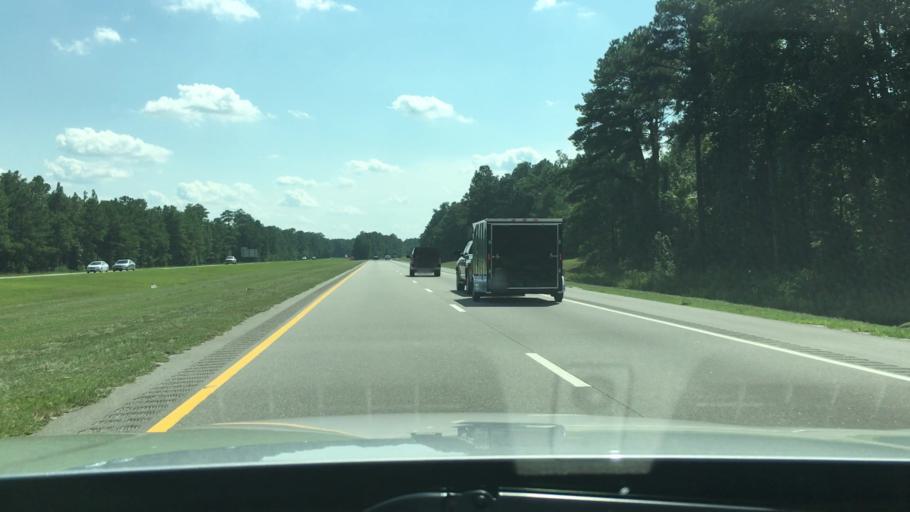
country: US
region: North Carolina
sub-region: Cumberland County
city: Hope Mills
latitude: 34.9511
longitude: -78.9022
